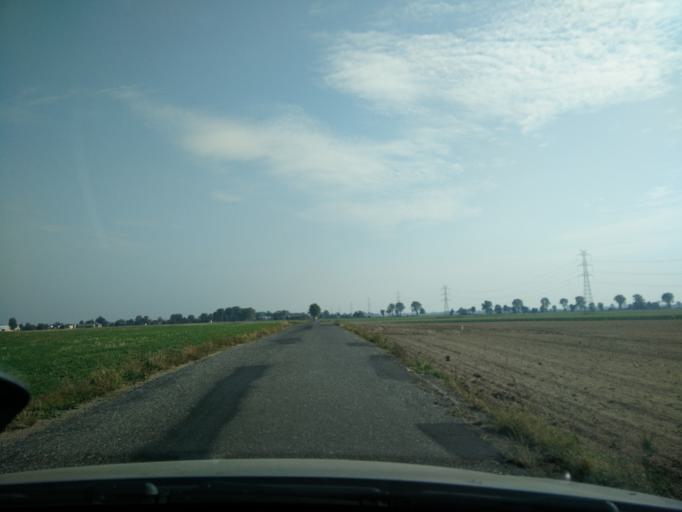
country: PL
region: Greater Poland Voivodeship
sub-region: Powiat sredzki
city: Sroda Wielkopolska
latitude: 52.3022
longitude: 17.2586
